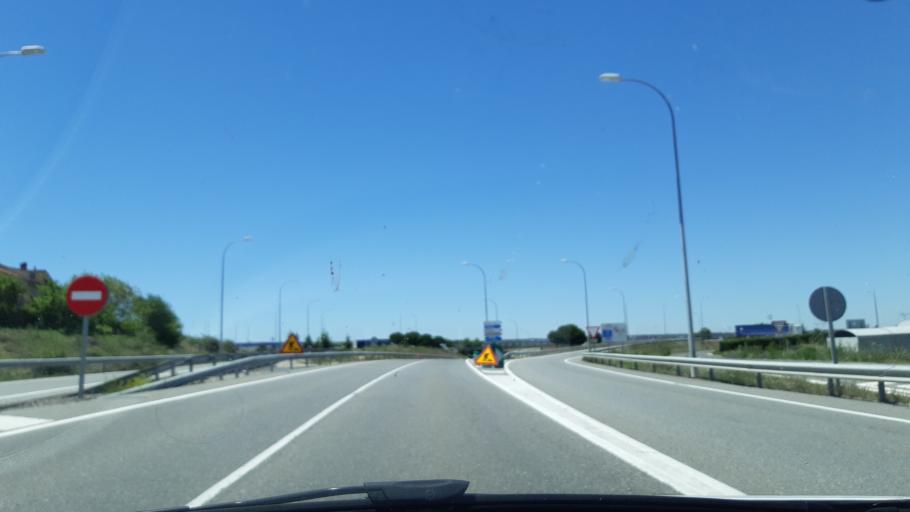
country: ES
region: Castille and Leon
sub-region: Provincia de Segovia
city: Villacastin
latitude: 40.7827
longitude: -4.4178
